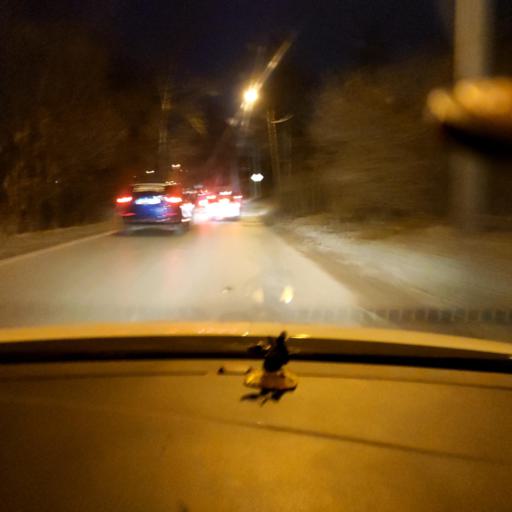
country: RU
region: Tatarstan
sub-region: Gorod Kazan'
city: Kazan
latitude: 55.7267
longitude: 49.1582
